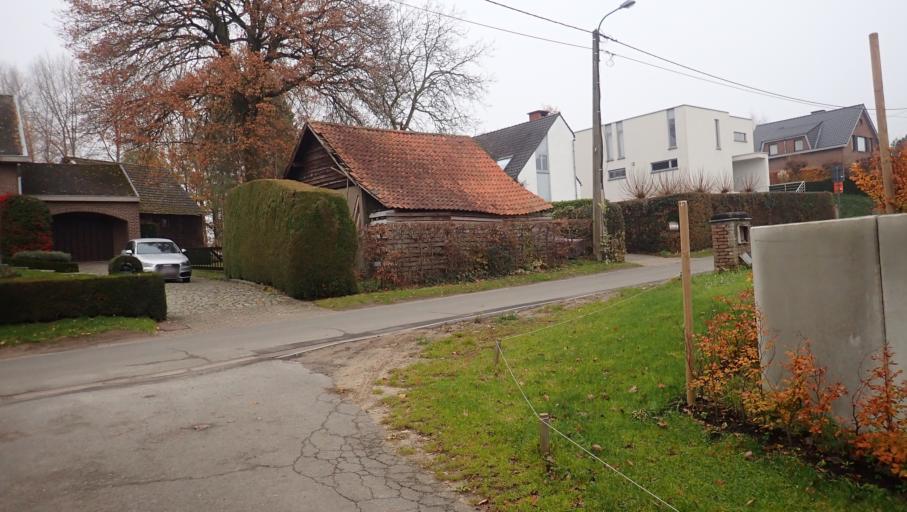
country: BE
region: Flanders
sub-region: Provincie Oost-Vlaanderen
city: Temse
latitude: 51.1255
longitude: 4.2413
